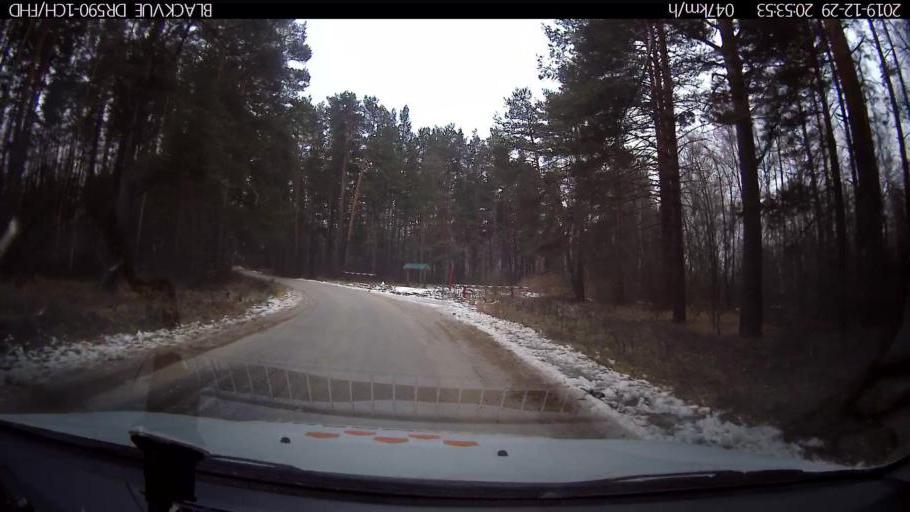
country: RU
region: Nizjnij Novgorod
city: Afonino
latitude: 56.1680
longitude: 43.9871
